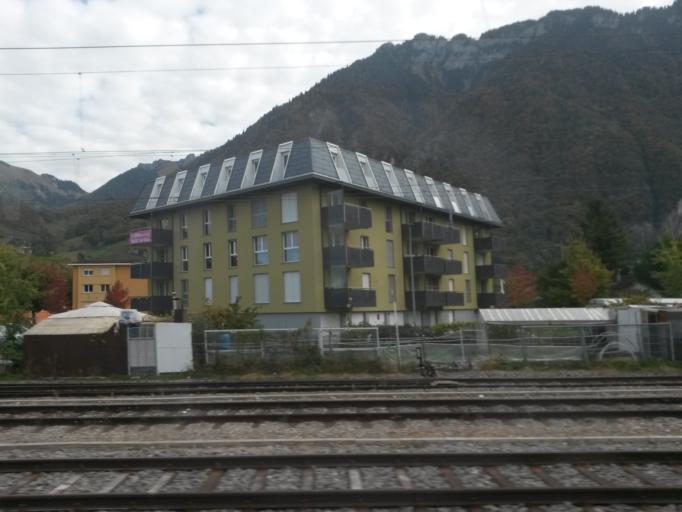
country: CH
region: Vaud
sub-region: Aigle District
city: Villeneuve
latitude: 46.3941
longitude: 6.9274
